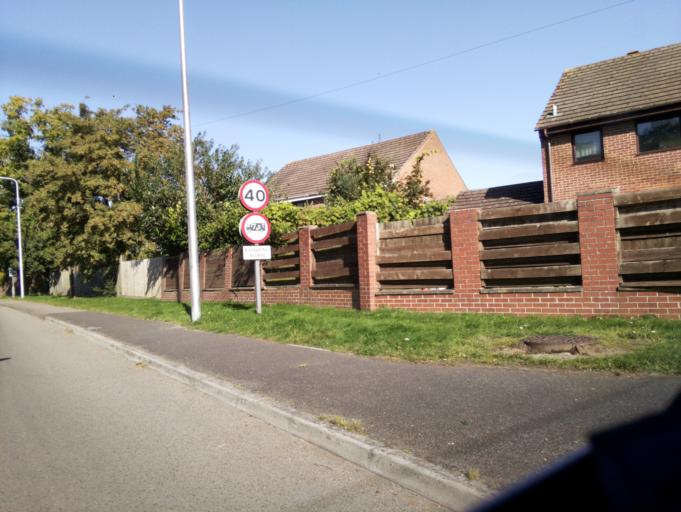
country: GB
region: England
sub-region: West Berkshire
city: Thatcham
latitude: 51.4123
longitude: -1.2637
